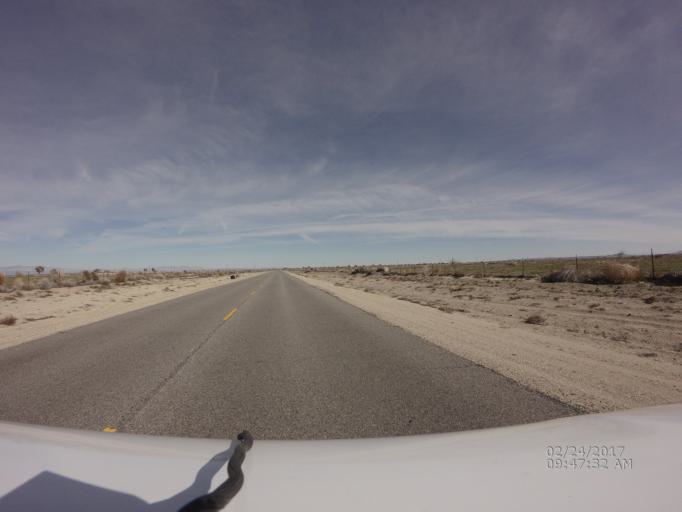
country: US
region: California
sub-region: Los Angeles County
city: Littlerock
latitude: 34.6245
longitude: -118.0053
